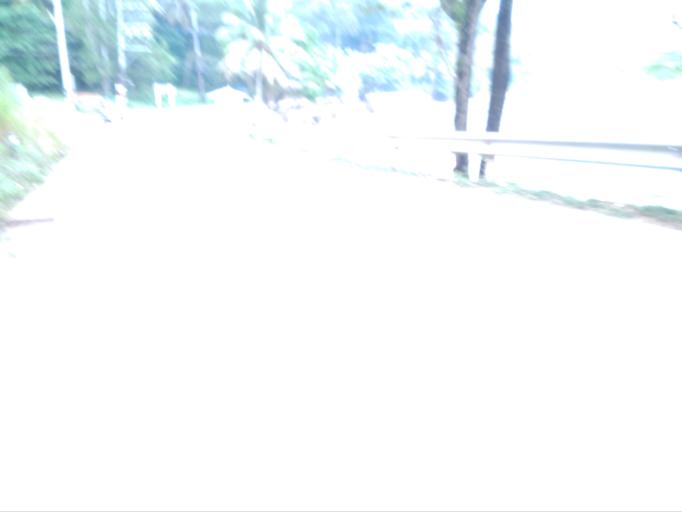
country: TH
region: Phangnga
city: Ko Yao
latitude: 8.1079
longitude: 98.6229
